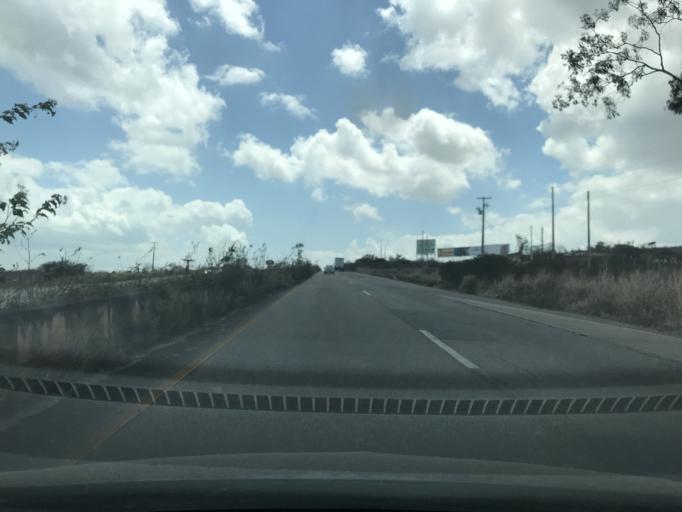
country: BR
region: Pernambuco
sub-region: Caruaru
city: Caruaru
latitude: -8.3041
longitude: -35.9281
